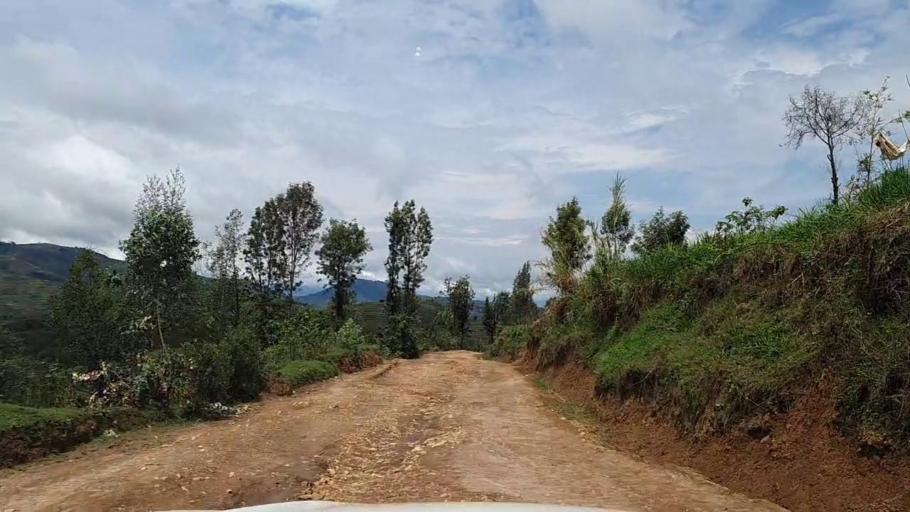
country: RW
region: Southern Province
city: Gikongoro
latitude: -2.3405
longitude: 29.5124
